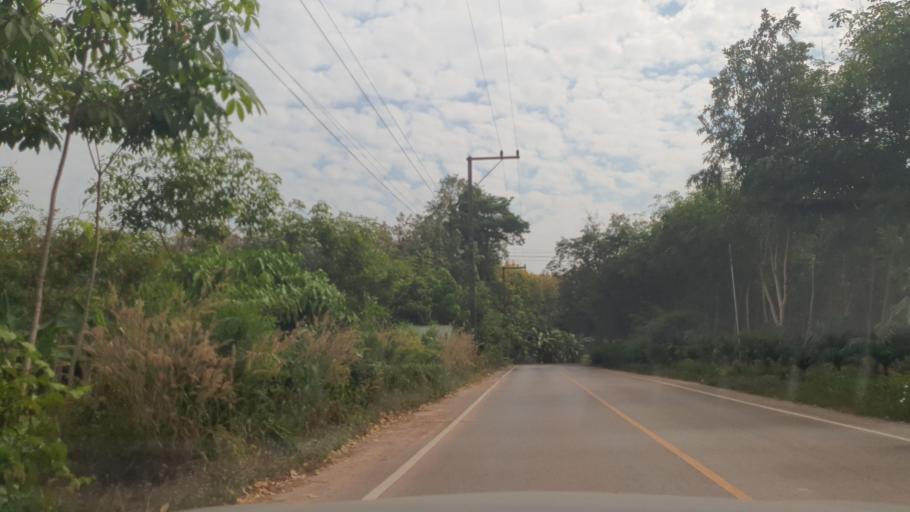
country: TH
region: Changwat Bueng Kan
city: Si Wilai
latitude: 18.2810
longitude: 103.7923
